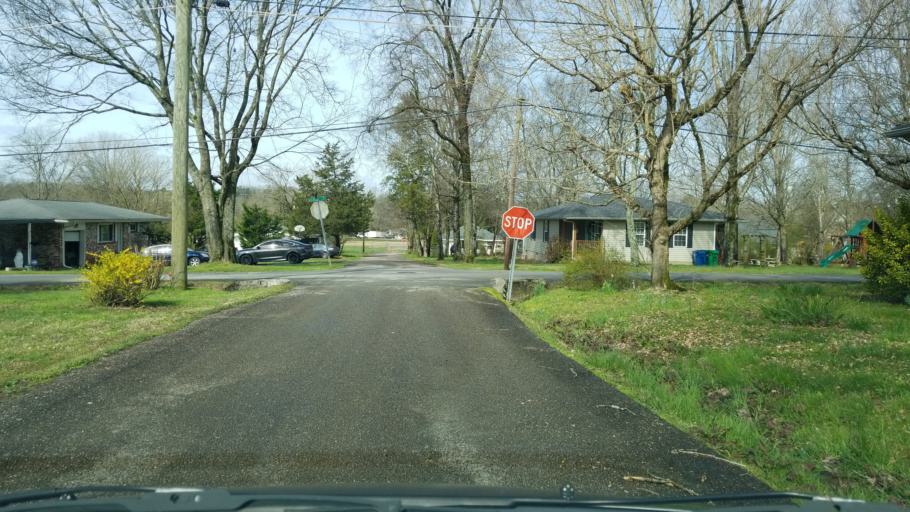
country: US
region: Tennessee
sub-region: Hamilton County
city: Collegedale
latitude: 35.0703
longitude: -85.0611
